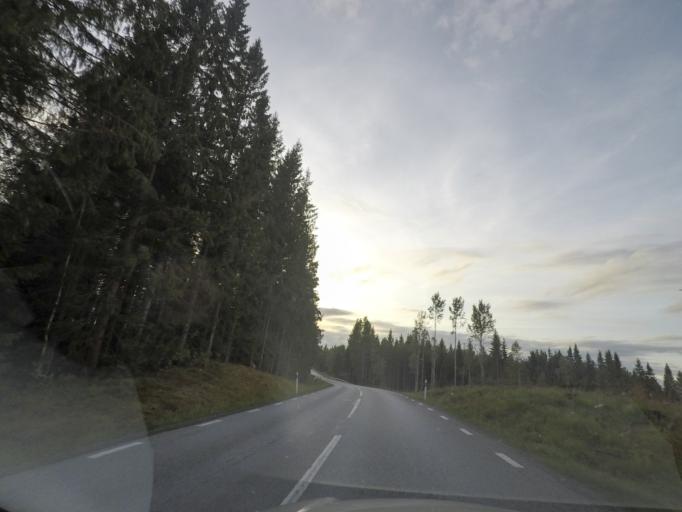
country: SE
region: OErebro
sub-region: Hallefors Kommun
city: Haellefors
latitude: 59.5910
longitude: 14.6890
